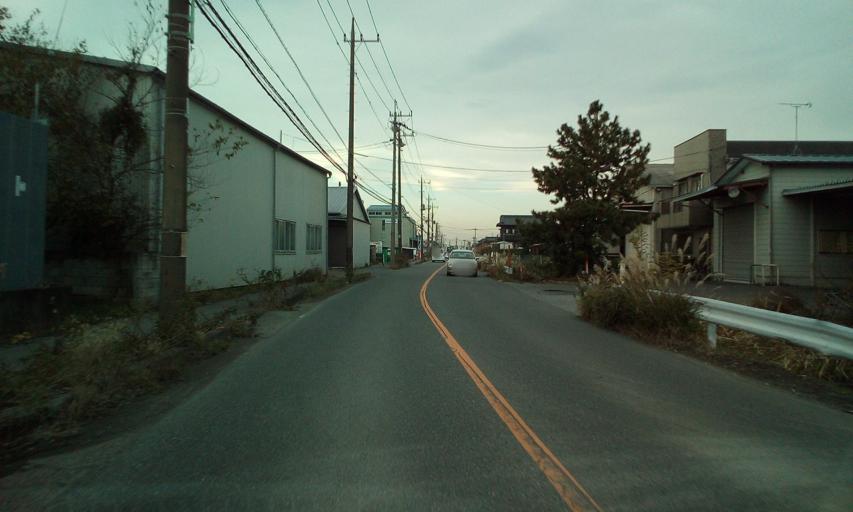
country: JP
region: Saitama
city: Yashio-shi
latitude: 35.8442
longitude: 139.8643
